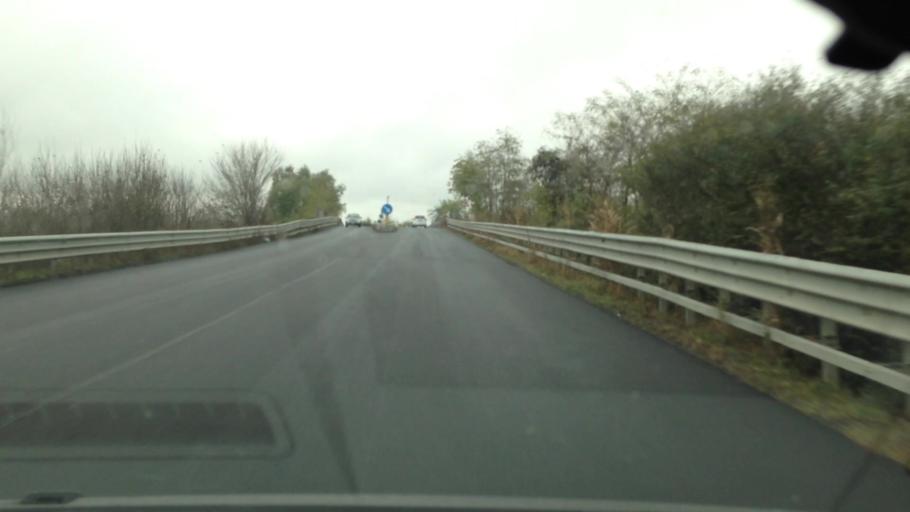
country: IT
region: Piedmont
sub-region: Provincia di Asti
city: Villanova d'Asti
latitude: 44.9631
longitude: 7.9075
